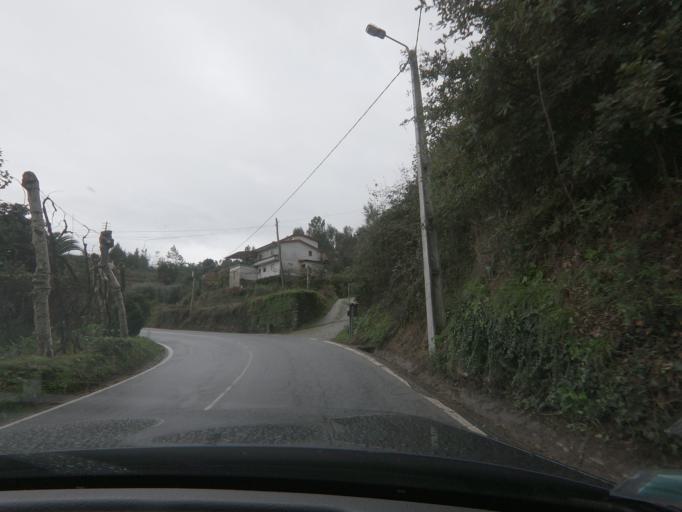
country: PT
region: Braga
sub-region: Celorico de Basto
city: Celorico de Basto
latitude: 41.4098
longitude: -7.9958
